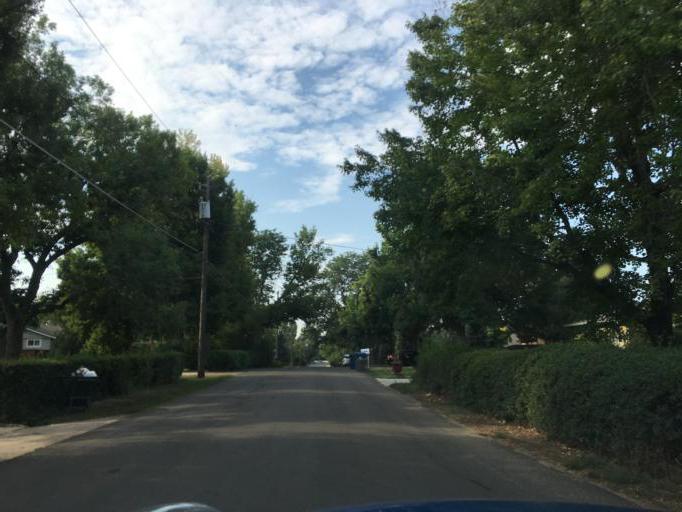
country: US
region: Colorado
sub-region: Jefferson County
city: Wheat Ridge
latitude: 39.7508
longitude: -105.1021
